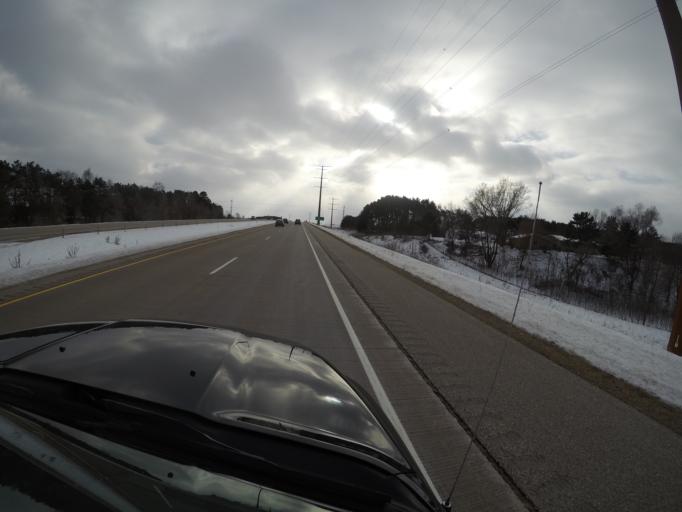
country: US
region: Wisconsin
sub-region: La Crosse County
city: Holmen
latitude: 43.9729
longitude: -91.2863
